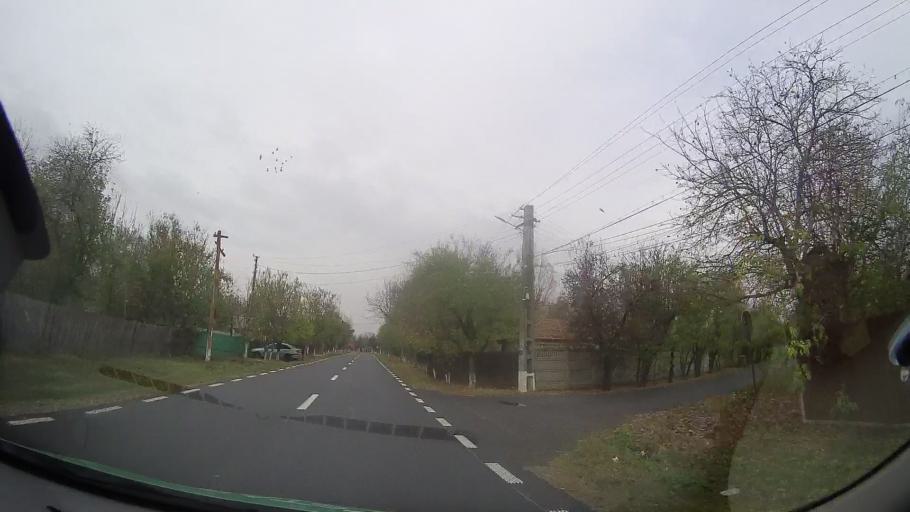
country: RO
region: Ilfov
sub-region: Comuna Nuci
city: Nuci
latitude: 44.7212
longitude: 26.2954
